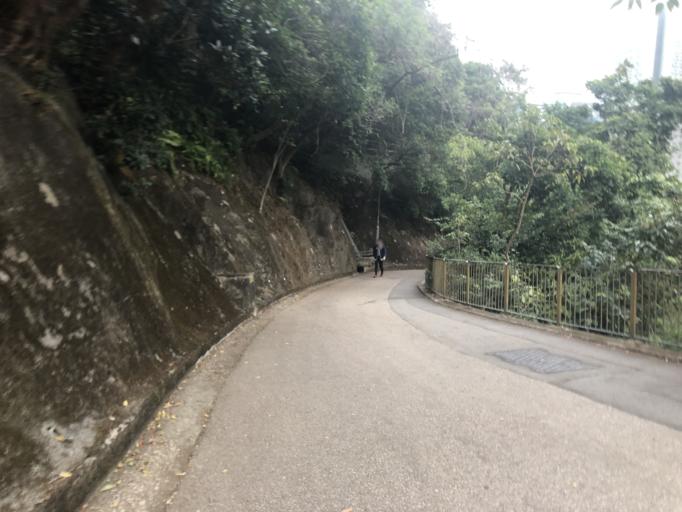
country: HK
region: Wanchai
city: Wan Chai
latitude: 22.2811
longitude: 114.2120
